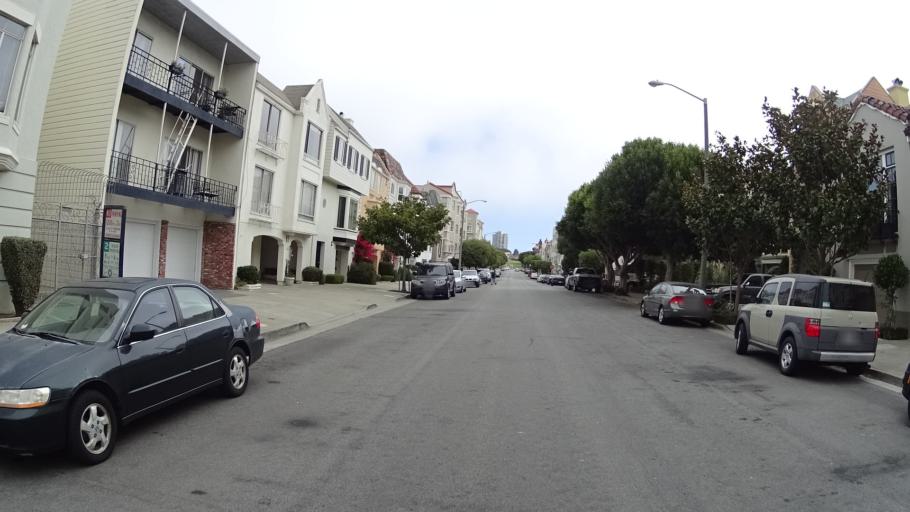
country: US
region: California
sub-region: San Francisco County
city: San Francisco
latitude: 37.8037
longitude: -122.4365
